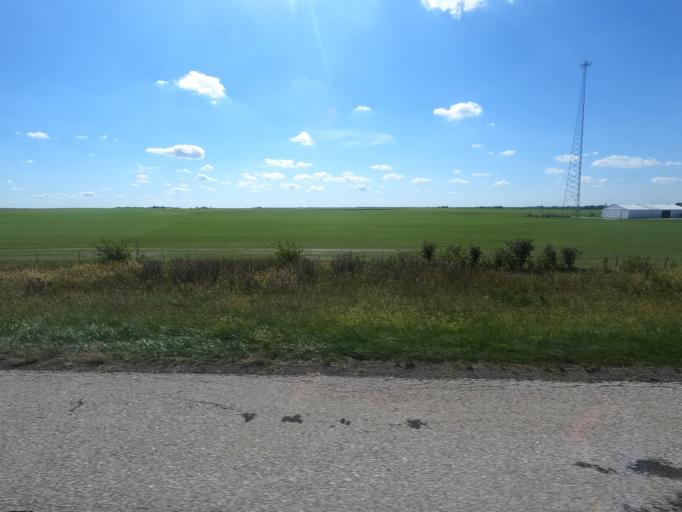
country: US
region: Illinois
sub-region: Washington County
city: Nashville
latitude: 38.3904
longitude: -89.2538
